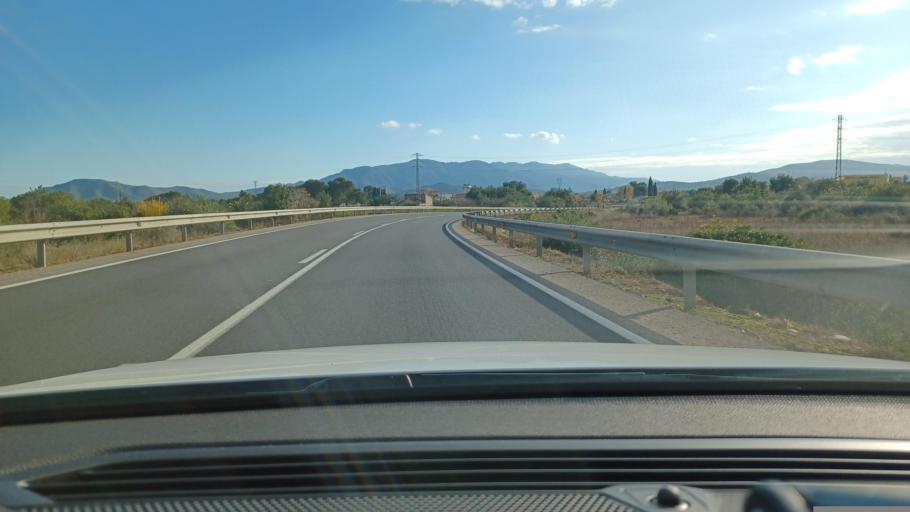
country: ES
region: Catalonia
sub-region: Provincia de Tarragona
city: Santa Barbara
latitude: 40.7202
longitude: 0.5055
